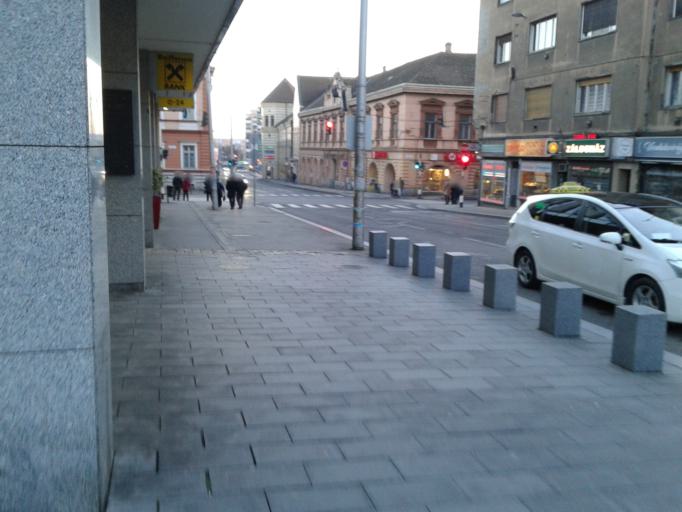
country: HU
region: Baranya
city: Pecs
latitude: 46.0736
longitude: 18.2293
